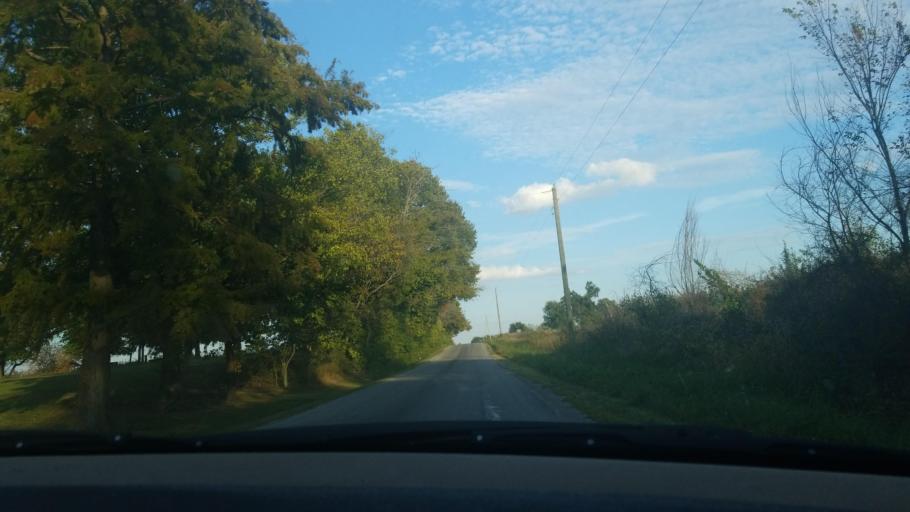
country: US
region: Illinois
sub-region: Saline County
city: Carrier Mills
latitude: 37.8050
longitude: -88.6820
